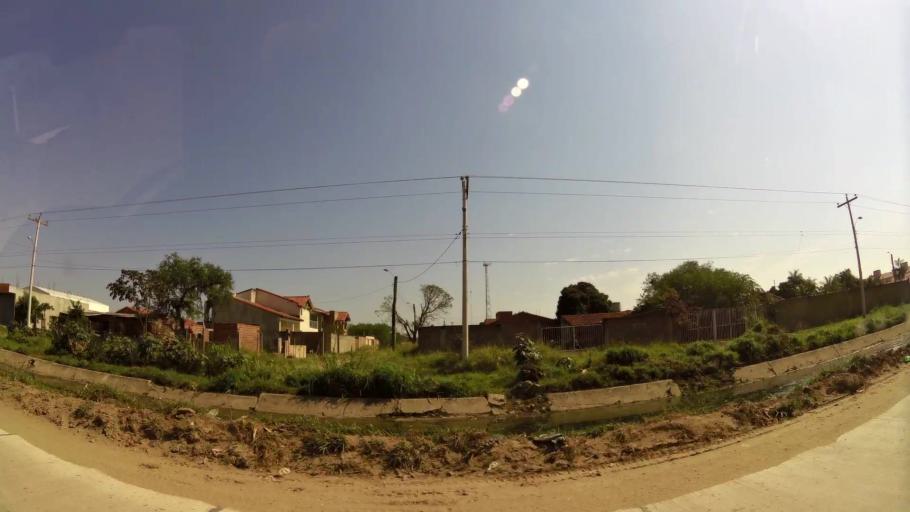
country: BO
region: Santa Cruz
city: Cotoca
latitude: -17.7601
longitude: -63.0910
